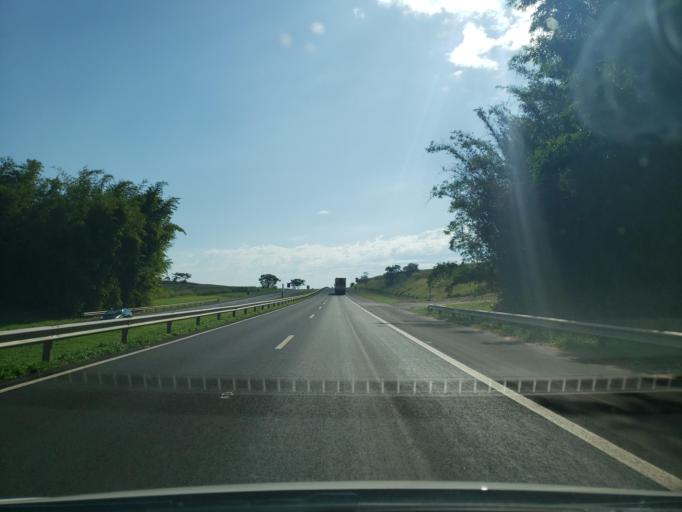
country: BR
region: Sao Paulo
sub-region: Promissao
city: Promissao
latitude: -21.5461
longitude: -49.9627
